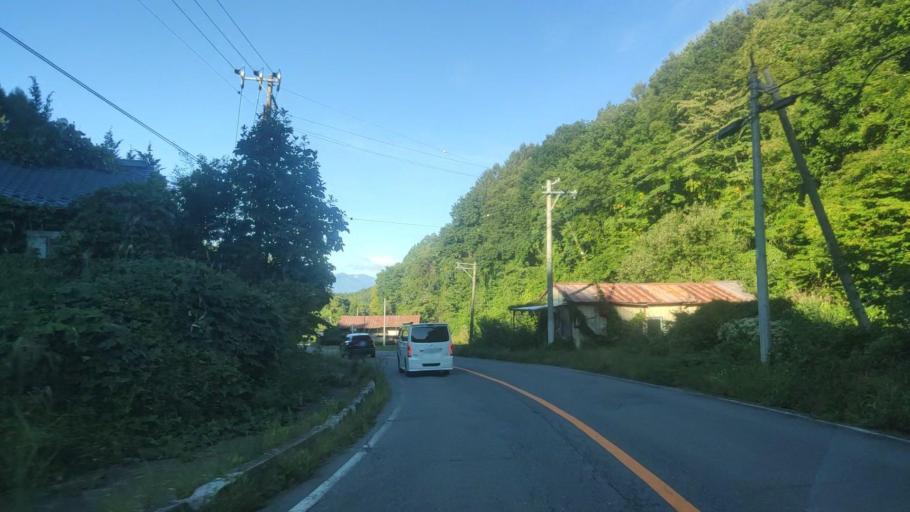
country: JP
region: Nagano
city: Kamimaruko
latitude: 36.2348
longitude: 138.3011
